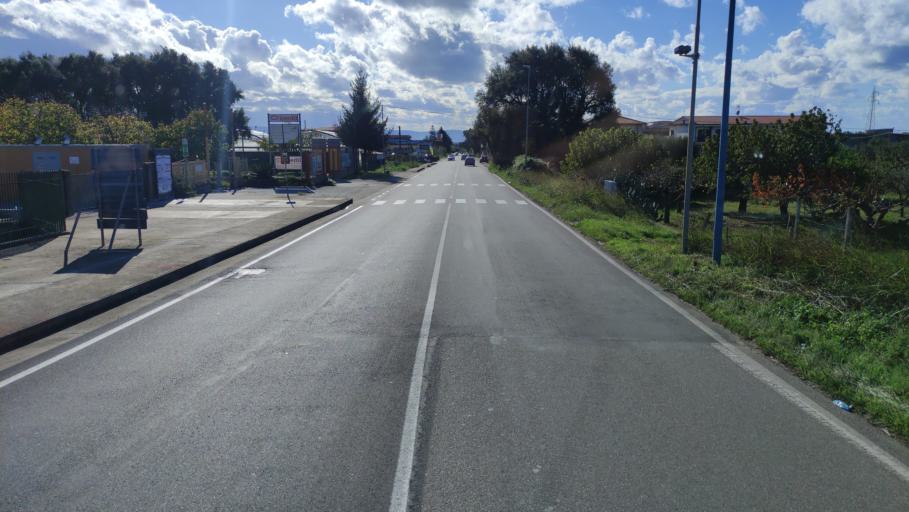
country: IT
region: Calabria
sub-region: Provincia di Catanzaro
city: Nicastro-Sambiase
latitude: 38.9345
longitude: 16.2884
